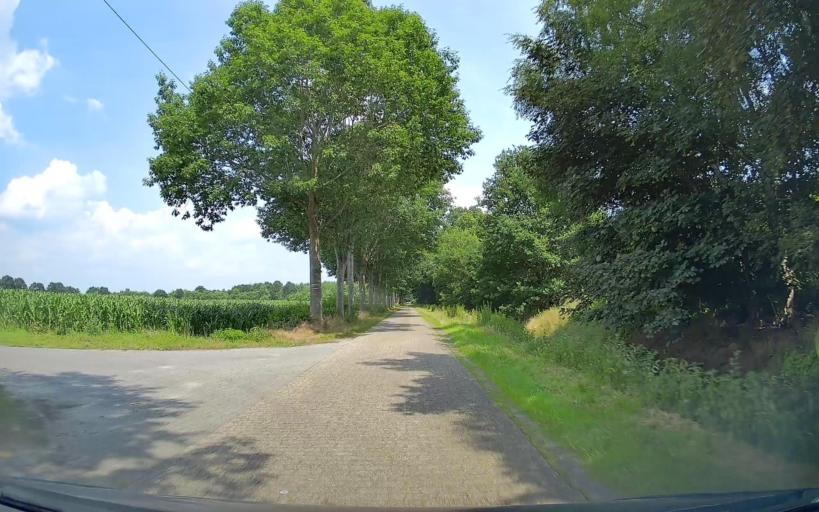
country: DE
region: Lower Saxony
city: Bosel
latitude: 53.0078
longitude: 7.9076
